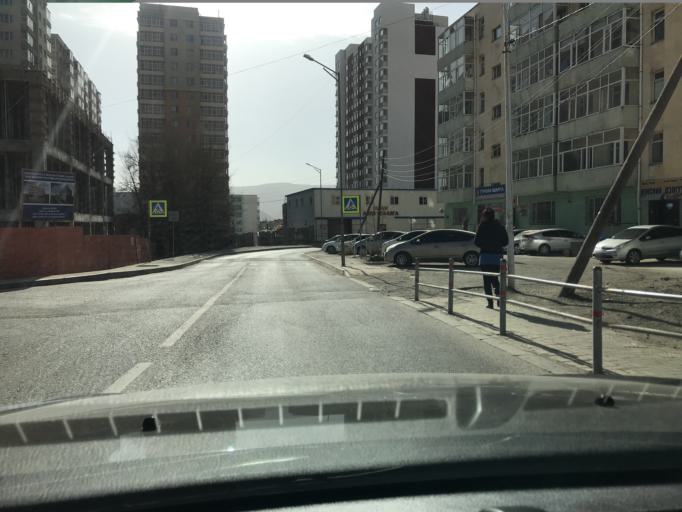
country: MN
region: Ulaanbaatar
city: Ulaanbaatar
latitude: 47.9214
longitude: 106.9607
